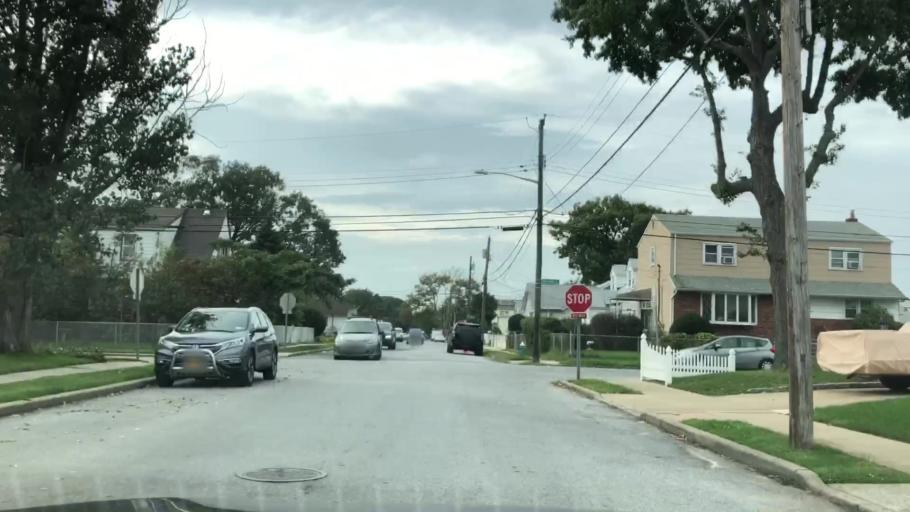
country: US
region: New York
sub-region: Nassau County
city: South Floral Park
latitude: 40.6998
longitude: -73.6943
